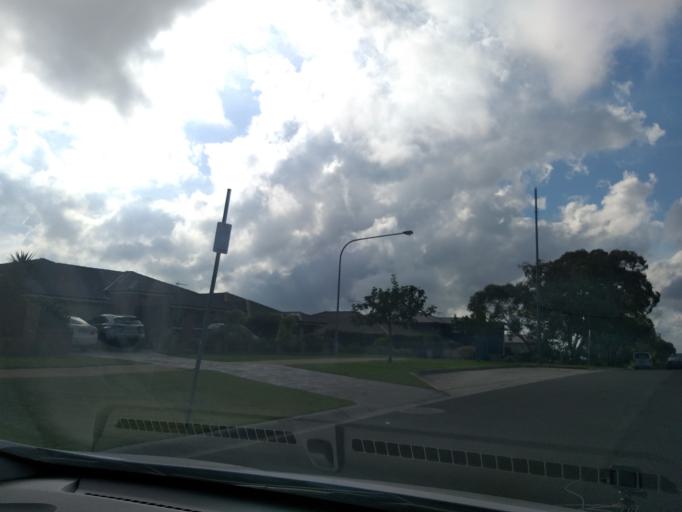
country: AU
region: New South Wales
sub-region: Wollongong
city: Helensburgh
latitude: -34.2010
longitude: 150.9800
